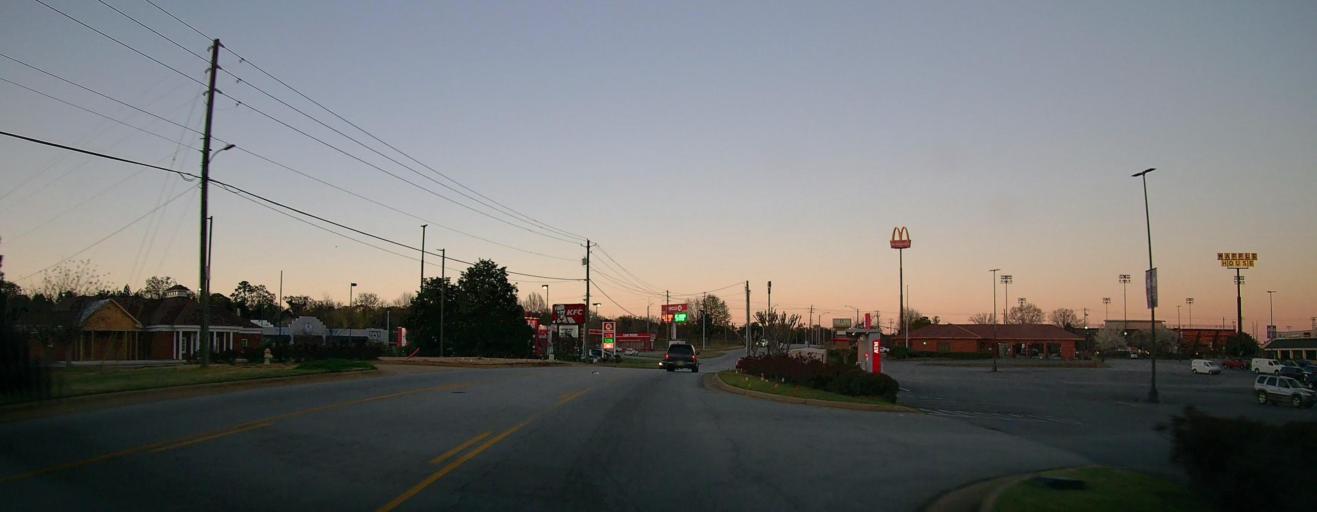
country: US
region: Alabama
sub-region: Russell County
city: Phenix City
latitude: 32.4965
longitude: -85.0182
